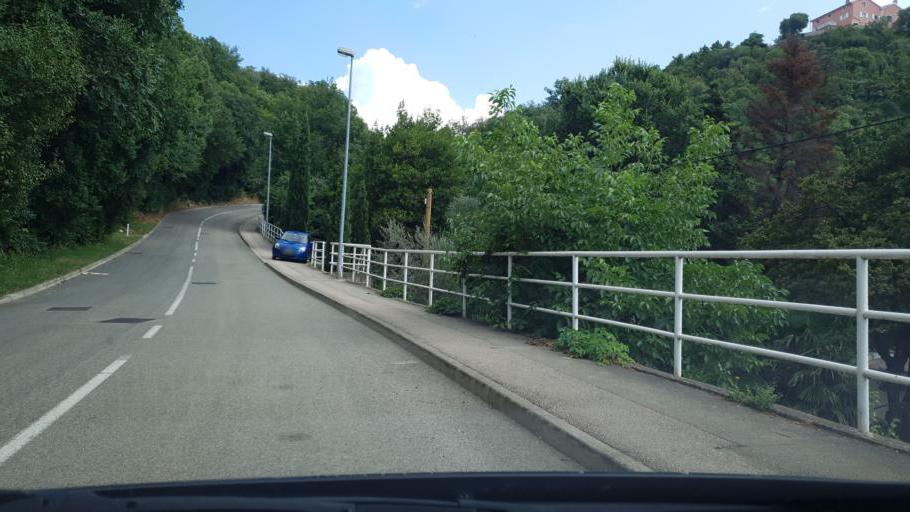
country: HR
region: Primorsko-Goranska
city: Omisalj
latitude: 45.2151
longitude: 14.5541
